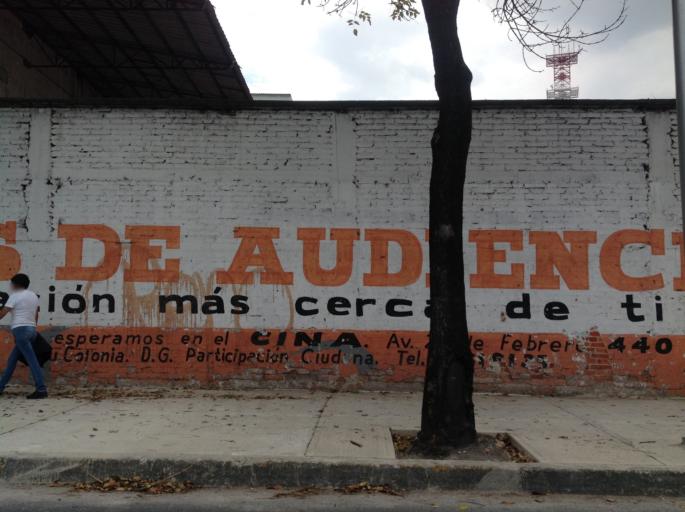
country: MX
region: Mexico City
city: Azcapotzalco
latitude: 19.4725
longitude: -99.1894
